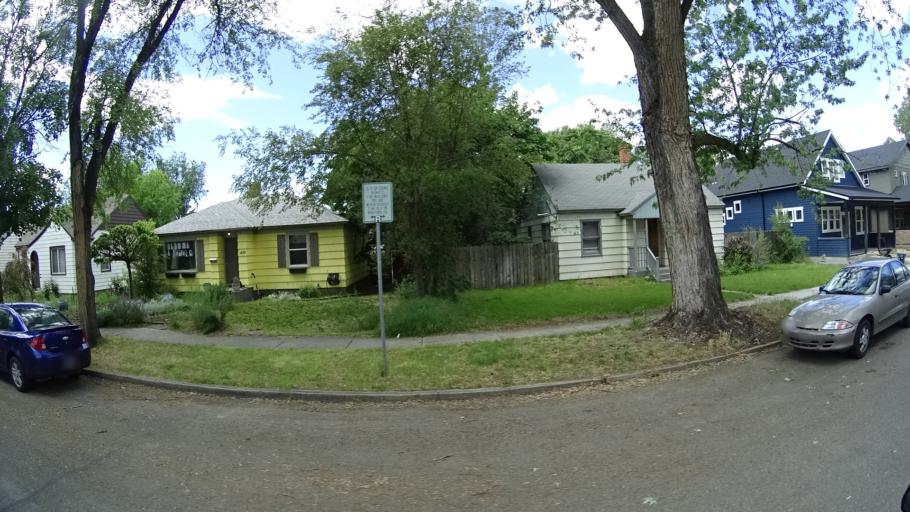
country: US
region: Idaho
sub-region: Ada County
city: Boise
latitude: 43.5951
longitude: -116.1986
